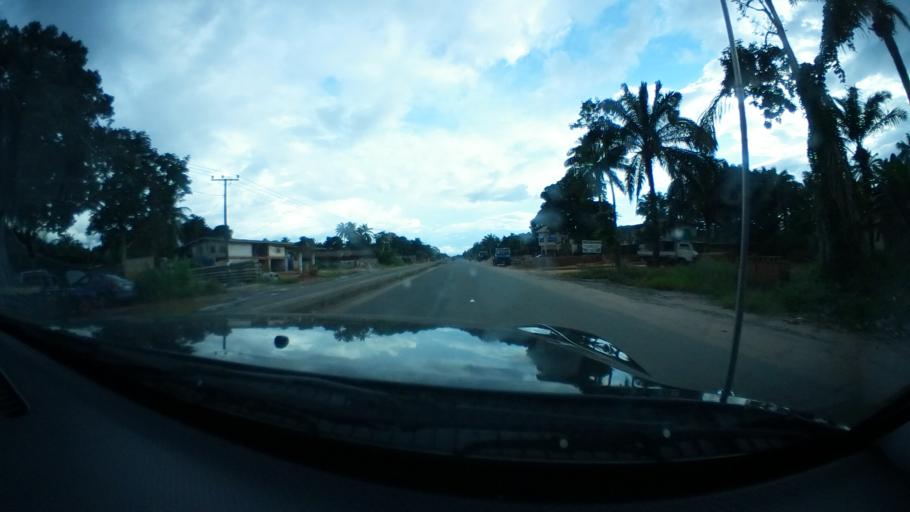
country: NG
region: Imo
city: Orlu
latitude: 5.7809
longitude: 7.0152
